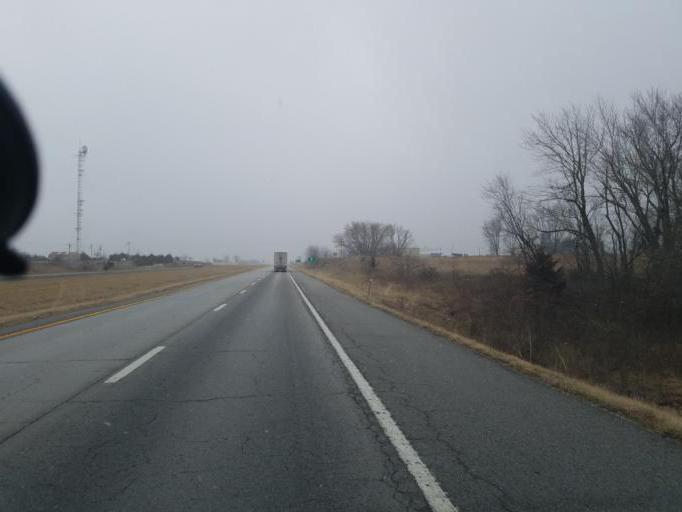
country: US
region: Missouri
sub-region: Macon County
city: La Plata
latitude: 39.9224
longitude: -92.4752
